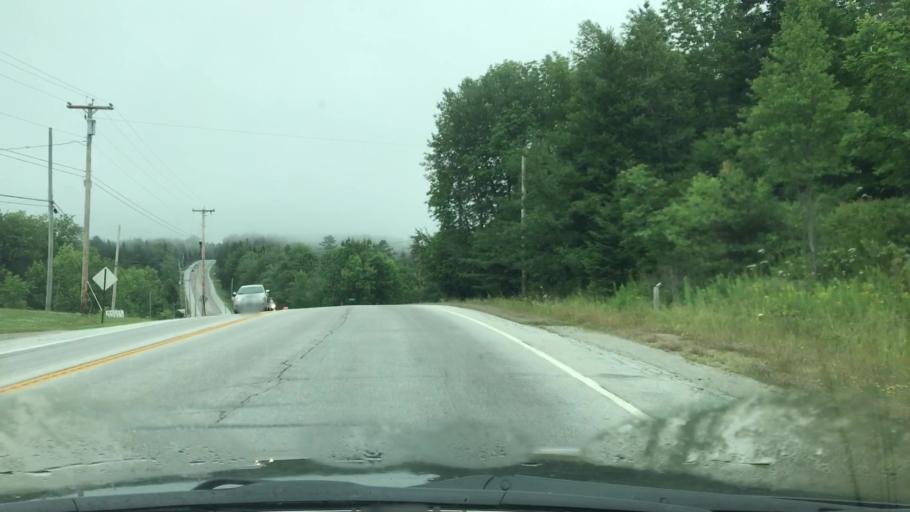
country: US
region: Maine
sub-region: Waldo County
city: Northport
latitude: 44.3039
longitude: -68.9781
